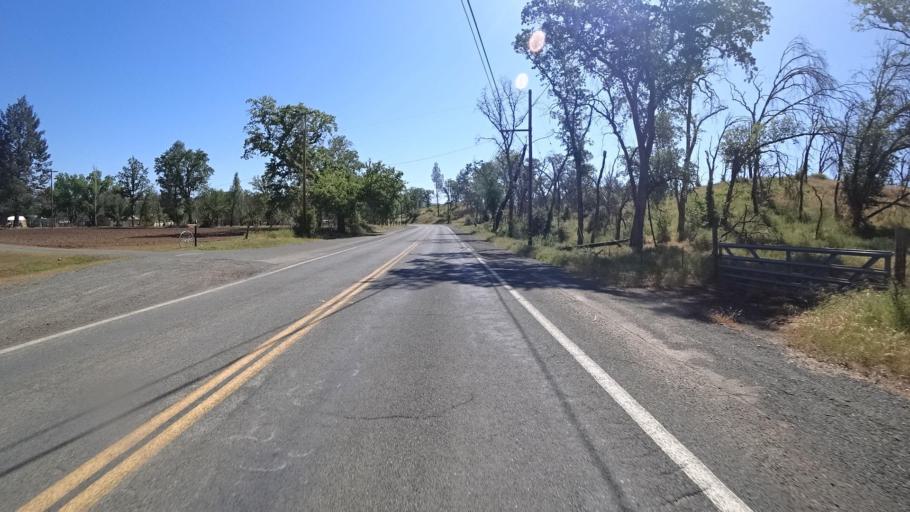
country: US
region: California
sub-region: Lake County
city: Lower Lake
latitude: 38.9081
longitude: -122.5940
